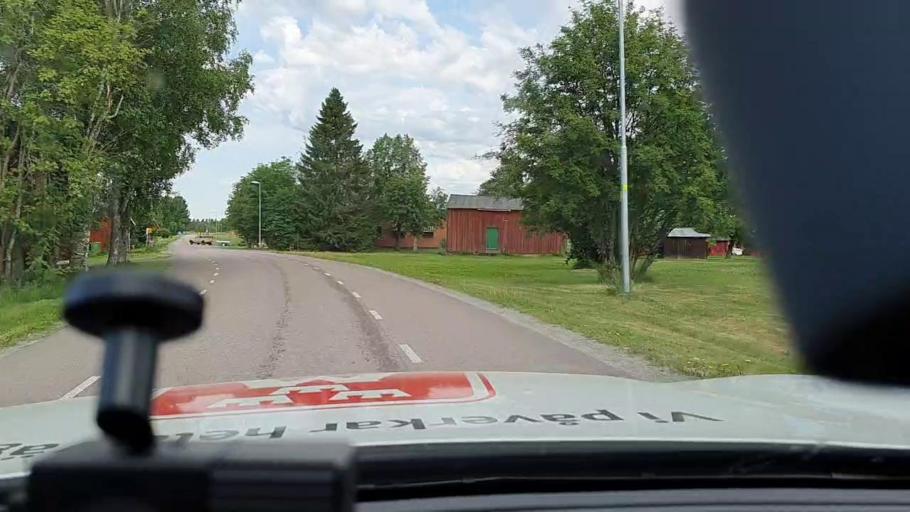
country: SE
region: Norrbotten
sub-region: Bodens Kommun
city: Saevast
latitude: 65.6838
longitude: 21.7970
